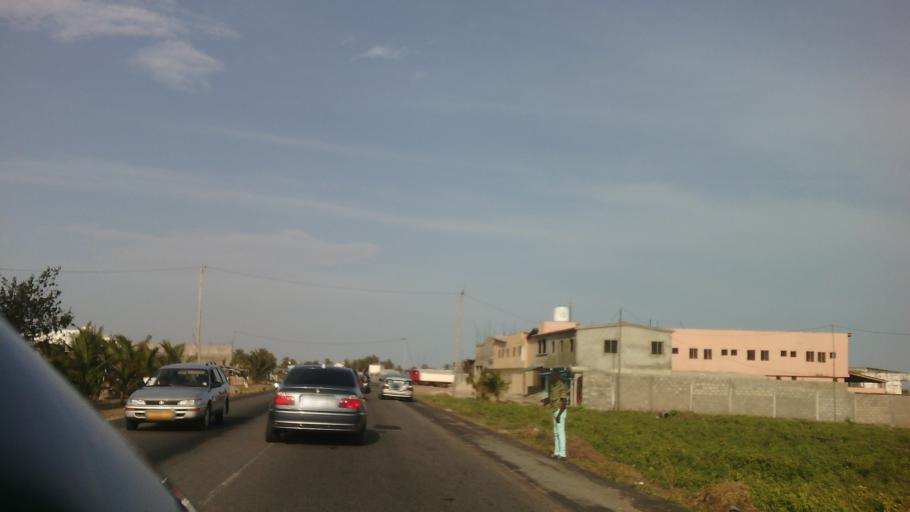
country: TG
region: Maritime
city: Lome
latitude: 6.1802
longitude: 1.3871
